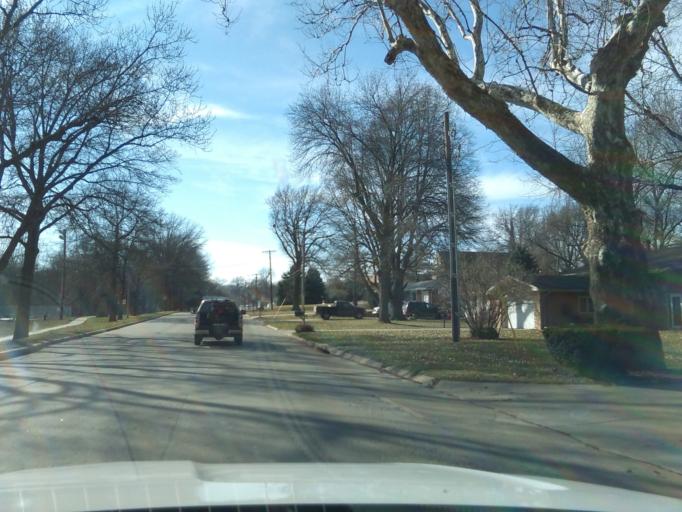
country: US
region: Nebraska
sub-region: Otoe County
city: Nebraska City
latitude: 40.6769
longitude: -95.8748
